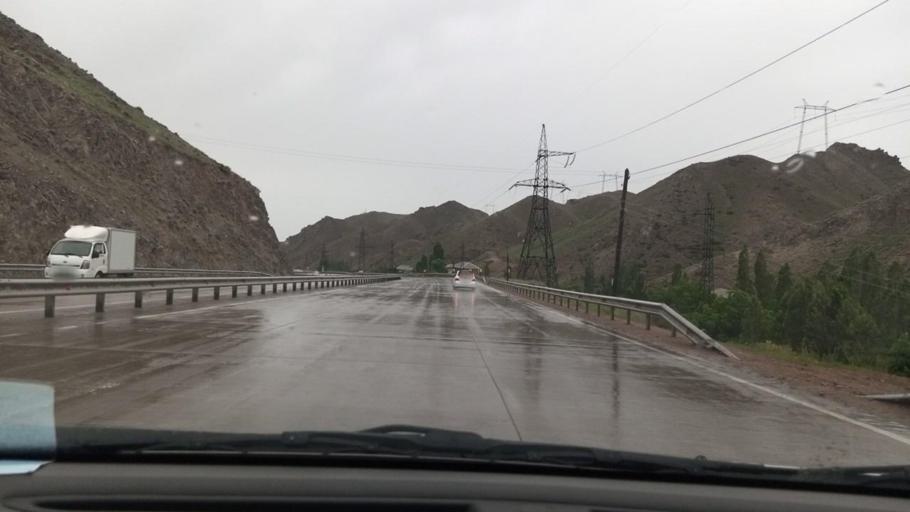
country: TJ
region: Viloyati Sughd
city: Shaydon
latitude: 40.9691
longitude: 70.6555
